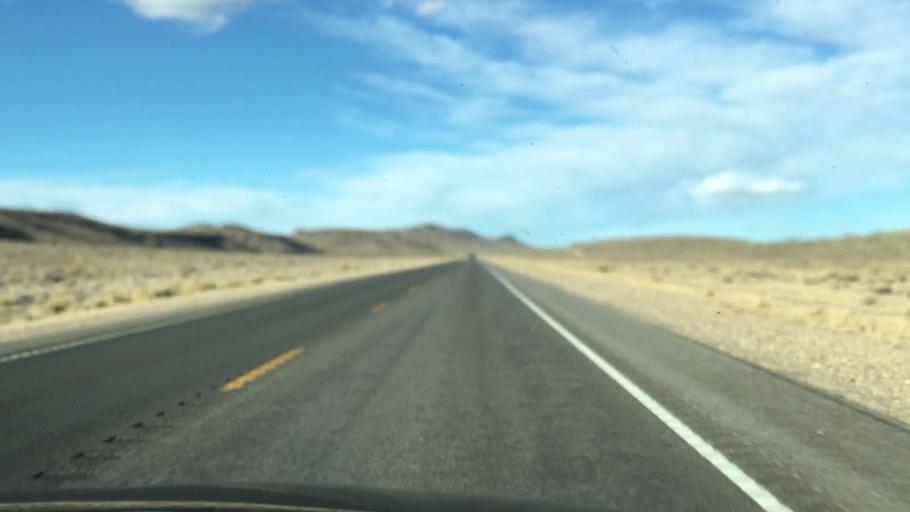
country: US
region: Nevada
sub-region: Esmeralda County
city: Goldfield
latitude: 37.6316
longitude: -117.2182
